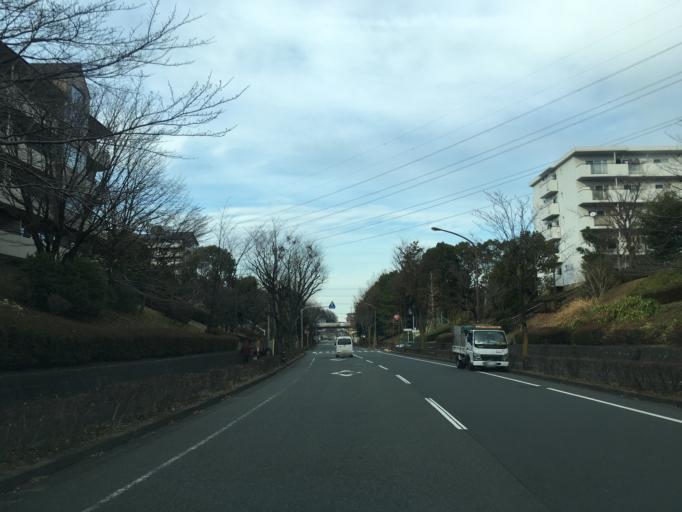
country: JP
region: Tokyo
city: Hino
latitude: 35.6192
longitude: 139.4374
